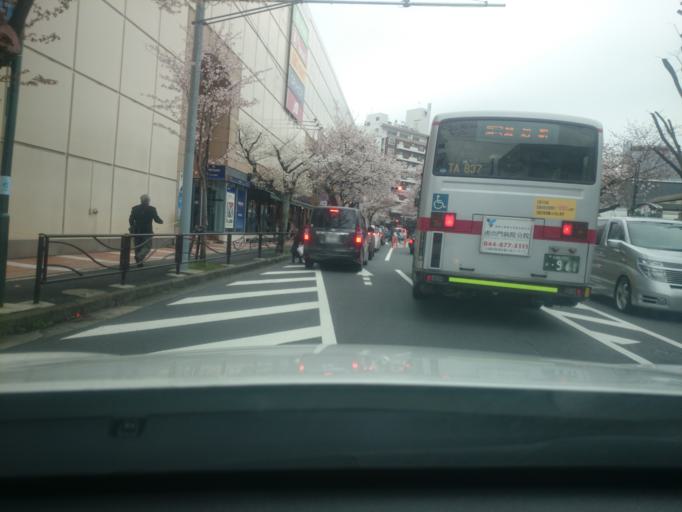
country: JP
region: Tokyo
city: Chofugaoka
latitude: 35.5792
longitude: 139.5738
